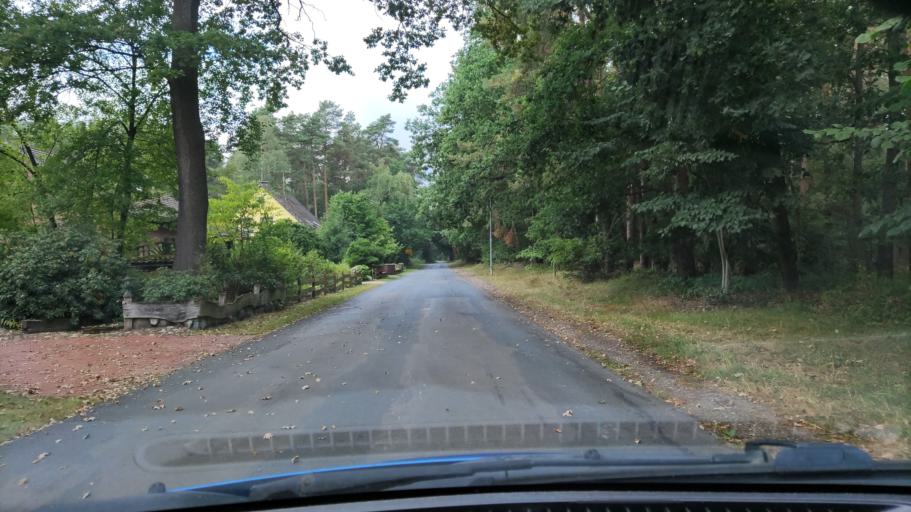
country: DE
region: Lower Saxony
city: Walsrode
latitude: 52.8273
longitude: 9.6158
